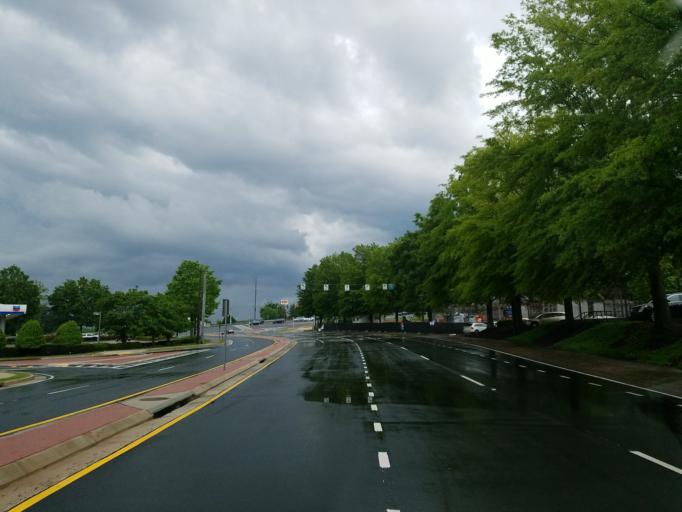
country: US
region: Georgia
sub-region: Cobb County
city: Kennesaw
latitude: 34.0359
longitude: -84.5751
